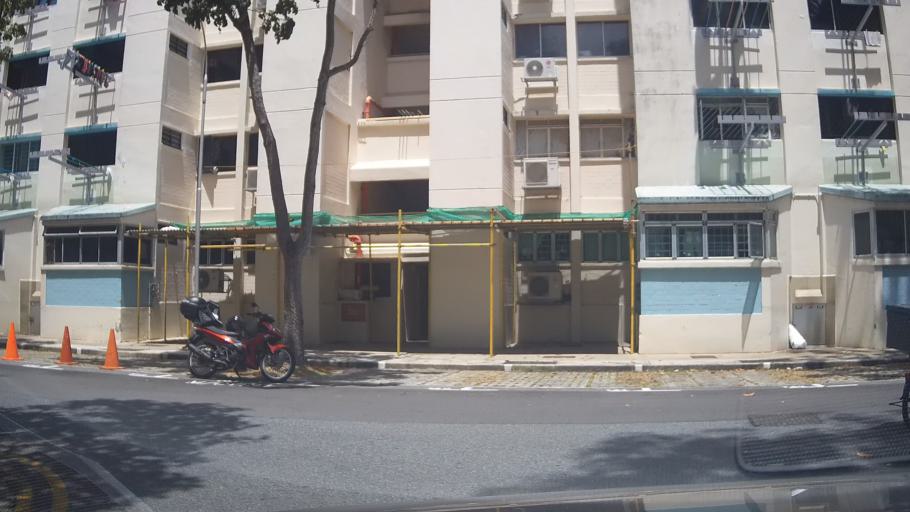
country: SG
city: Singapore
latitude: 1.3574
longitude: 103.9543
